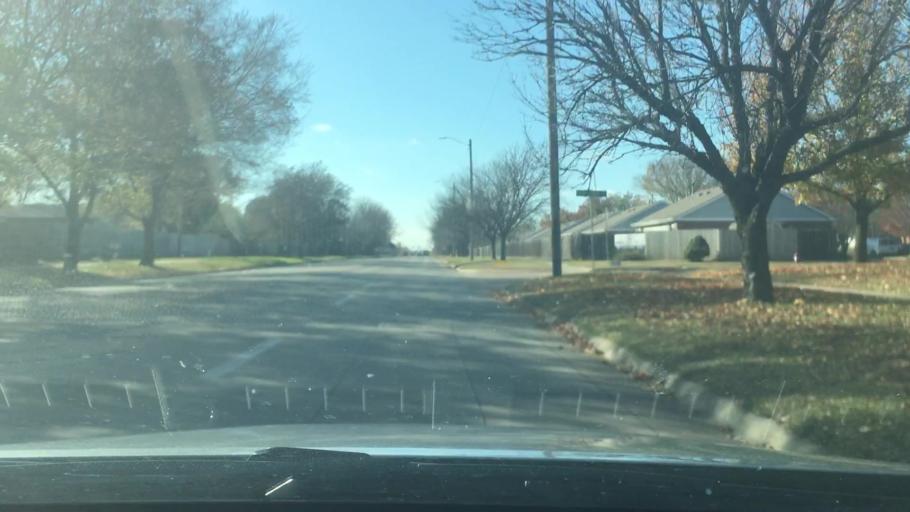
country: US
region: Kansas
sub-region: Sedgwick County
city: Maize
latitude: 37.6936
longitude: -97.4747
